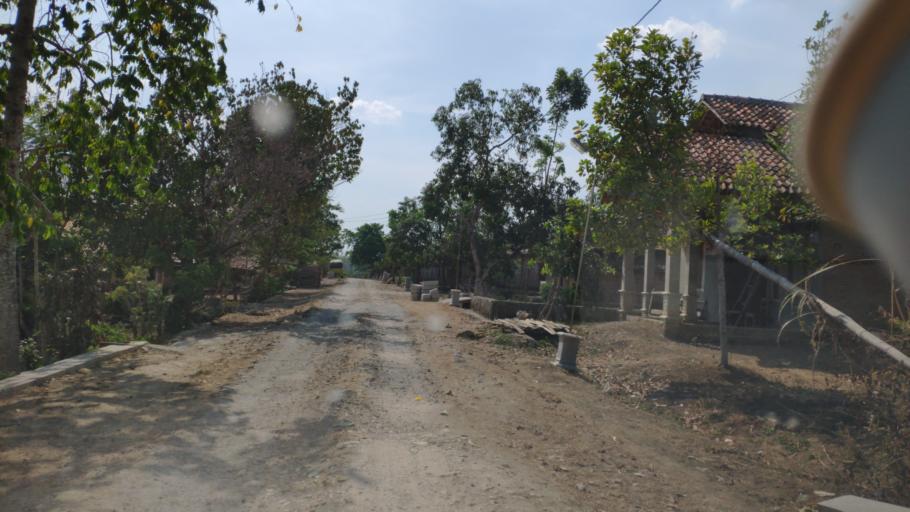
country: ID
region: Central Java
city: Plosorejo
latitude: -6.9962
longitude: 111.2658
